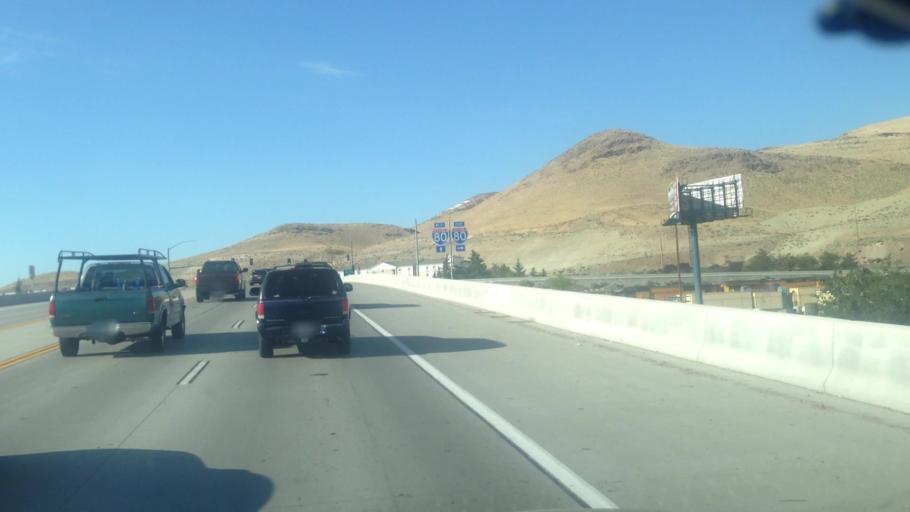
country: US
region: Nevada
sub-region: Washoe County
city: Sparks
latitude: 39.5242
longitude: -119.7014
